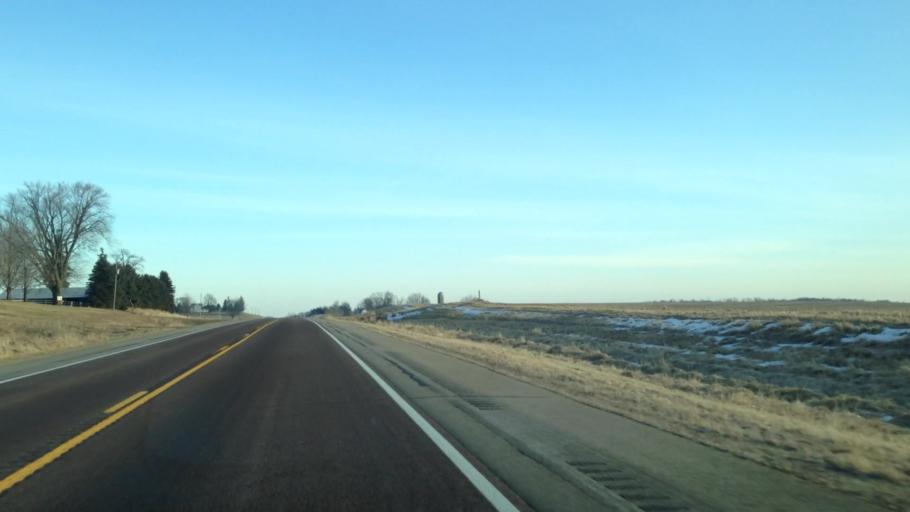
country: US
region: Minnesota
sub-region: Goodhue County
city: Zumbrota
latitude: 44.3304
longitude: -92.6442
